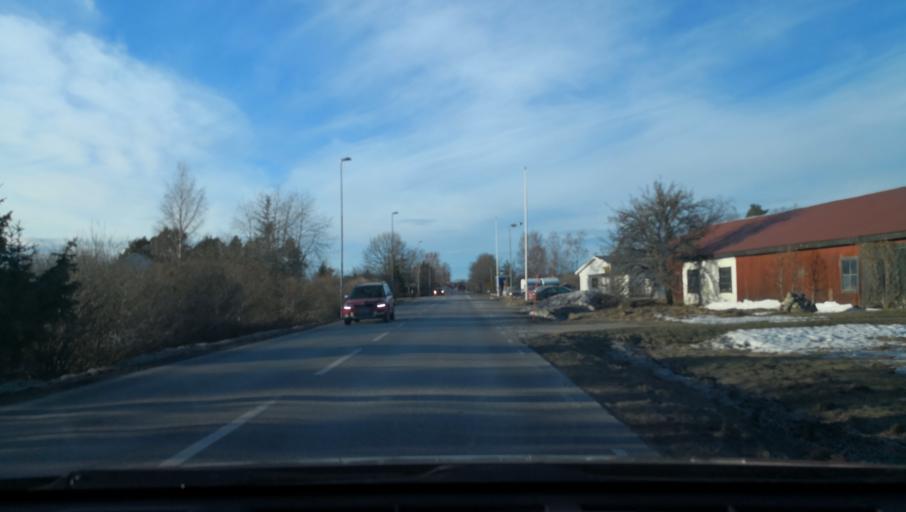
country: SE
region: Uppsala
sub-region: Osthammars Kommun
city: OEsthammar
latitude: 60.2832
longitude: 18.2931
